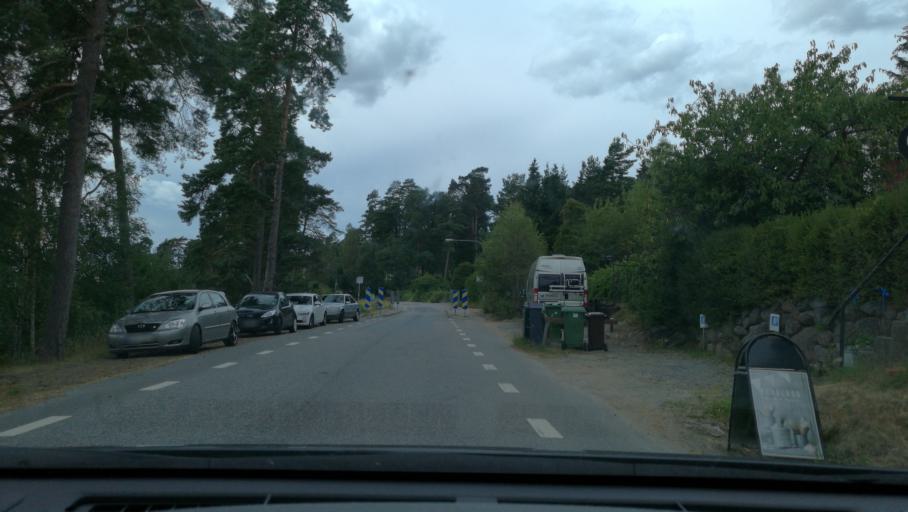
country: SE
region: OEstergoetland
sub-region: Norrkopings Kommun
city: Krokek
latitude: 58.6668
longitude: 16.3437
